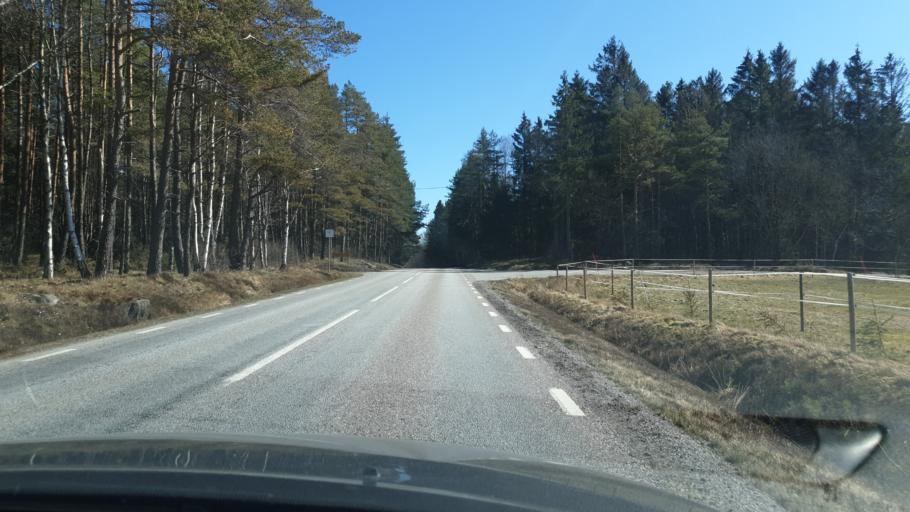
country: SE
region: Vaestra Goetaland
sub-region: Tanums Kommun
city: Tanumshede
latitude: 58.7418
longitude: 11.4677
